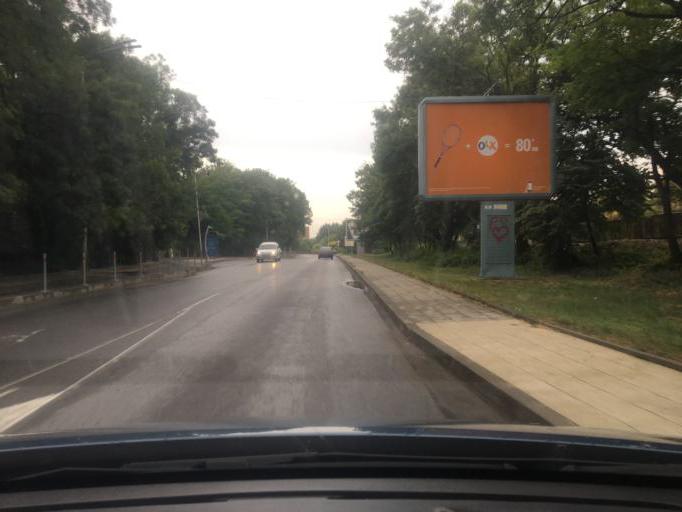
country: BG
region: Burgas
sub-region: Obshtina Burgas
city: Burgas
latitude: 42.5132
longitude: 27.4724
